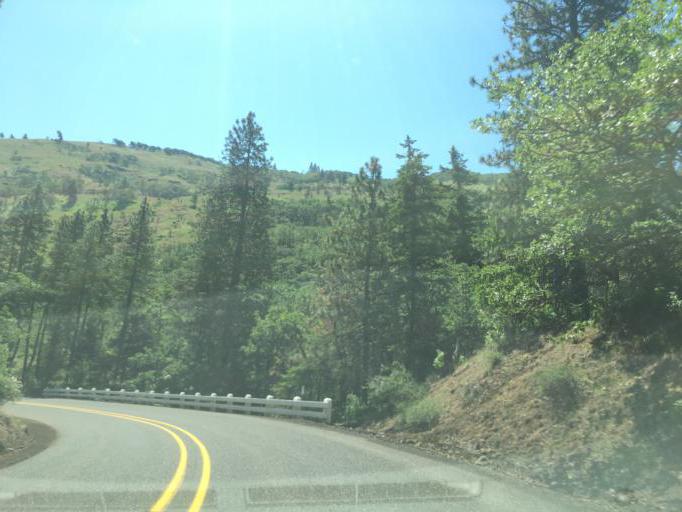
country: US
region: Oregon
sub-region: Wasco County
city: Chenoweth
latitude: 45.6776
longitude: -121.2935
